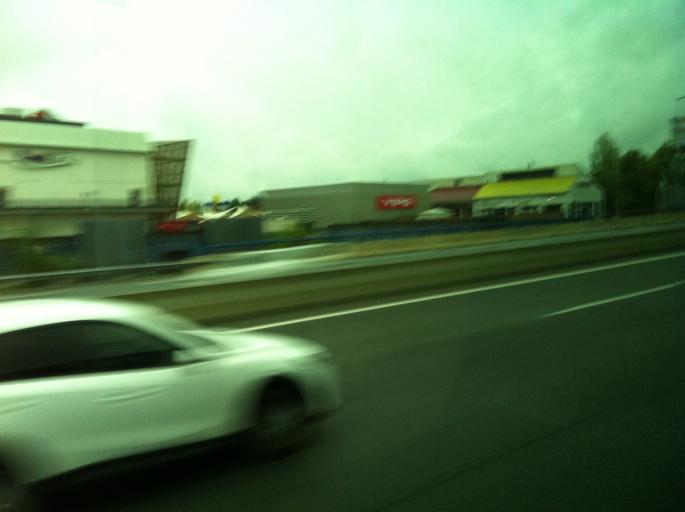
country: ES
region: Madrid
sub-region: Provincia de Madrid
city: Collado-Villalba
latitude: 40.6382
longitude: -4.0170
